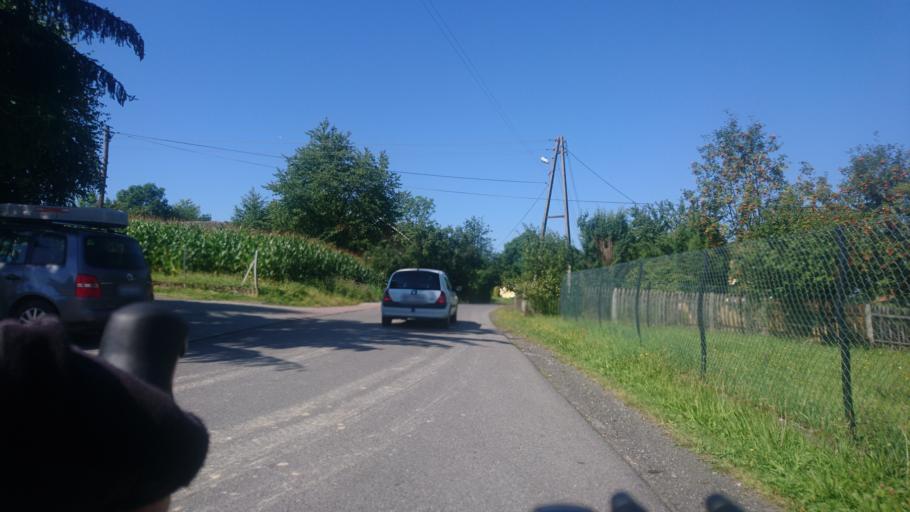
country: PL
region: Lesser Poland Voivodeship
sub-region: Powiat wadowicki
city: Laczany
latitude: 49.9534
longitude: 19.5765
